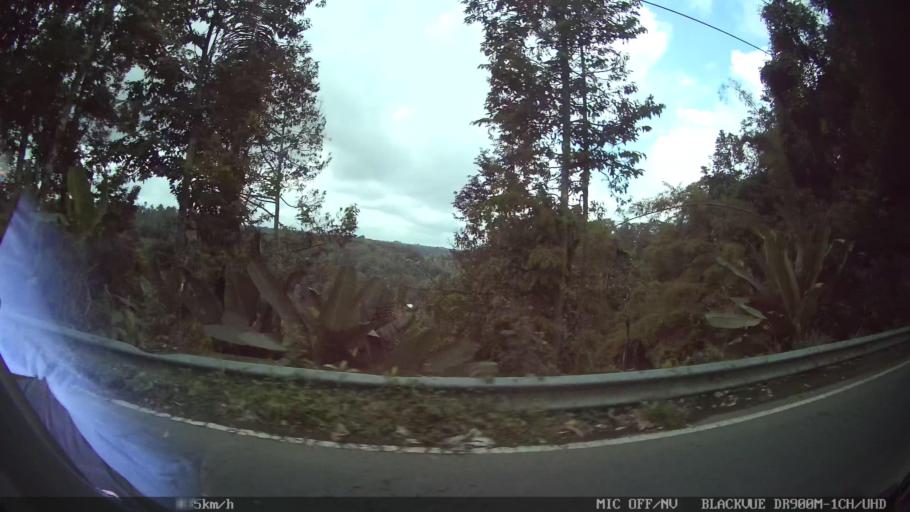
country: ID
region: Bali
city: Petang
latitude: -8.3702
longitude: 115.2244
